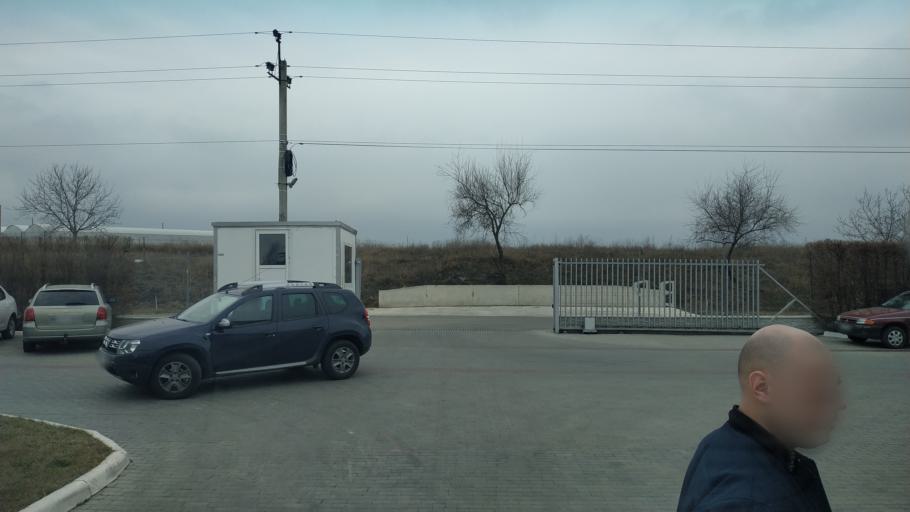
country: MD
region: Chisinau
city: Singera
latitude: 46.9082
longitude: 29.0084
